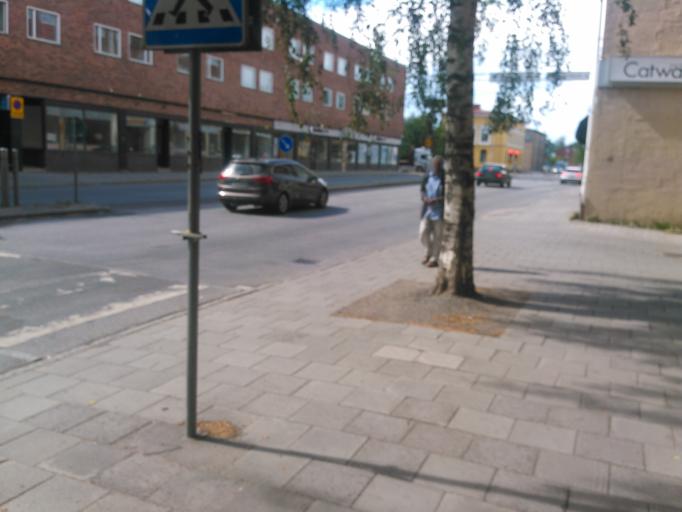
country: SE
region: Vaesterbotten
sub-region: Umea Kommun
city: Umea
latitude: 63.8259
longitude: 20.2578
